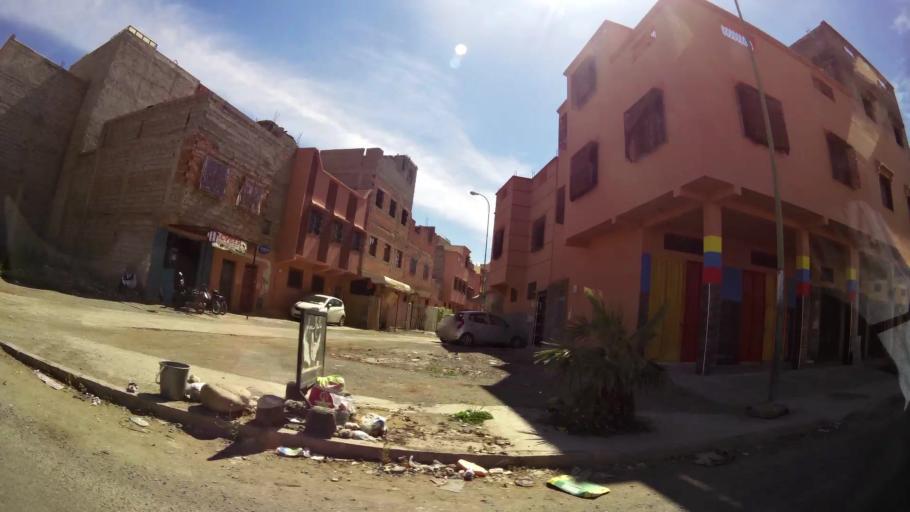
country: MA
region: Marrakech-Tensift-Al Haouz
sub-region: Marrakech
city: Marrakesh
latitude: 31.6400
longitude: -8.1078
